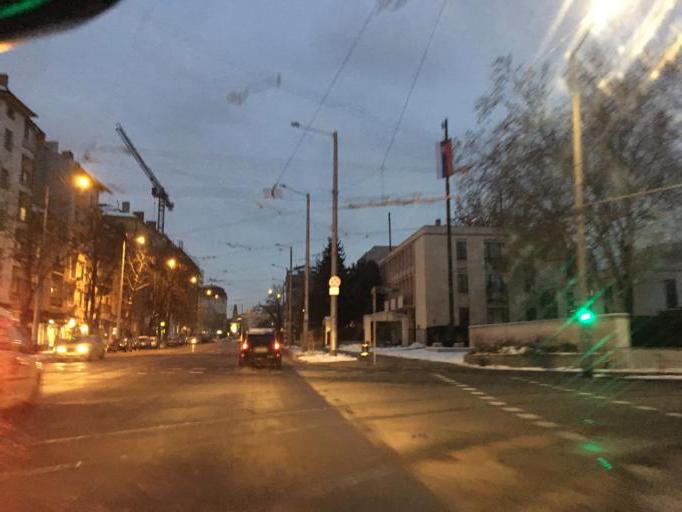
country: BG
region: Sofia-Capital
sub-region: Stolichna Obshtina
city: Sofia
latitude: 42.6966
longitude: 23.3382
